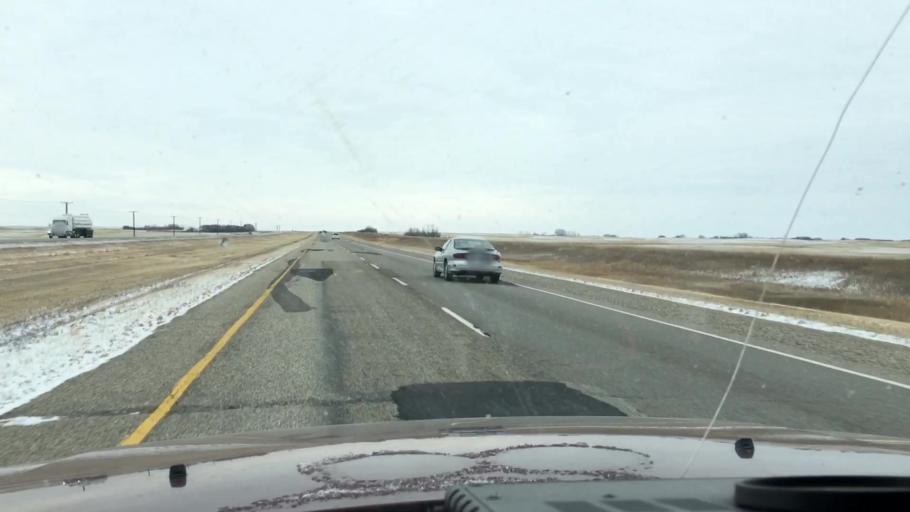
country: CA
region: Saskatchewan
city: Watrous
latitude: 51.4278
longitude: -106.1983
